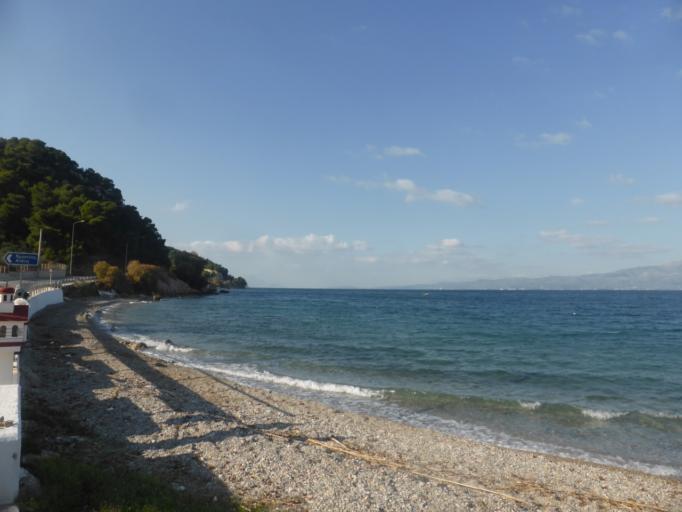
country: GR
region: Attica
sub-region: Nomarchia Anatolikis Attikis
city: Kalamos
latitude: 38.3071
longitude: 23.8553
